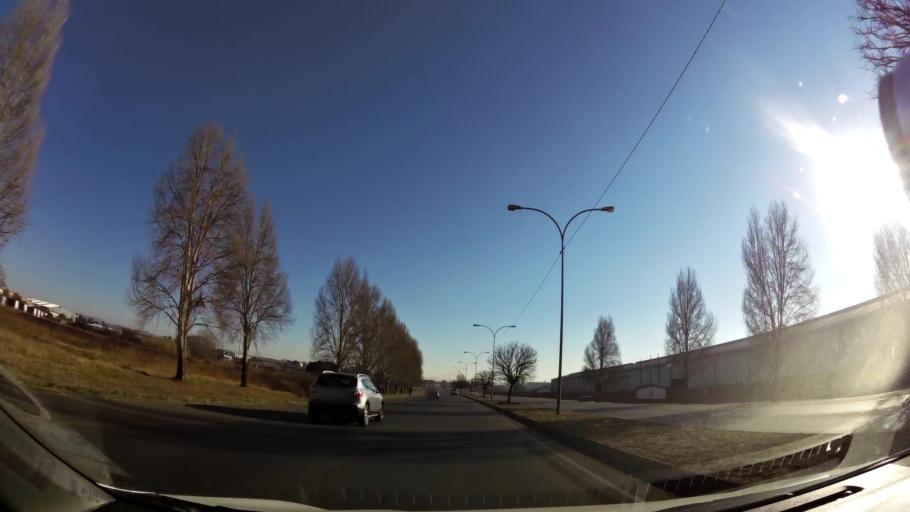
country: ZA
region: Gauteng
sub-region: Ekurhuleni Metropolitan Municipality
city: Germiston
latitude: -26.3099
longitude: 28.1387
